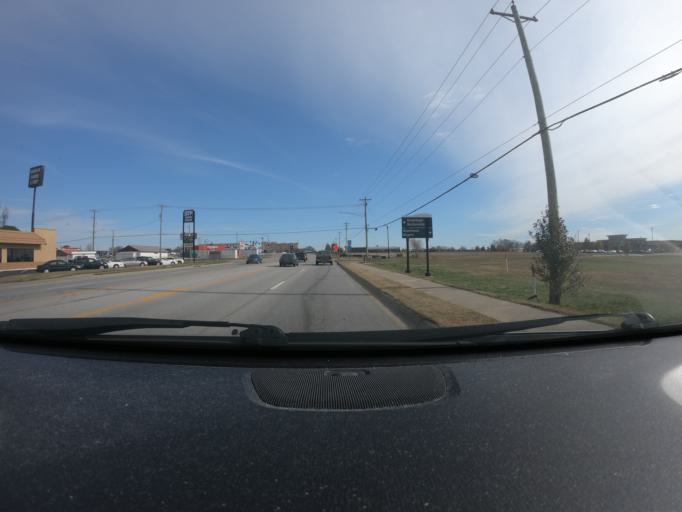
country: US
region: Arkansas
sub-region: Benton County
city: Bentonville
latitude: 36.3355
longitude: -94.2125
